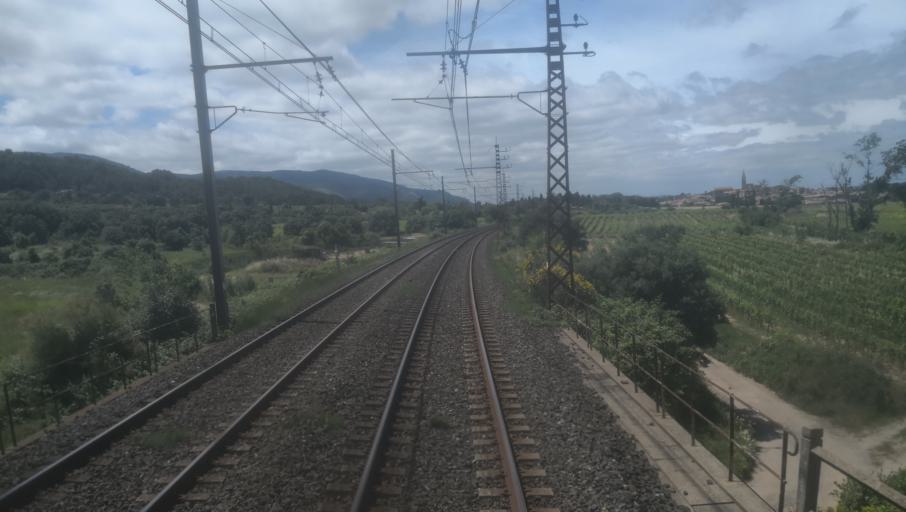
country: FR
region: Languedoc-Roussillon
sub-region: Departement de l'Aude
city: Capendu
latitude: 43.1817
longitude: 2.5727
